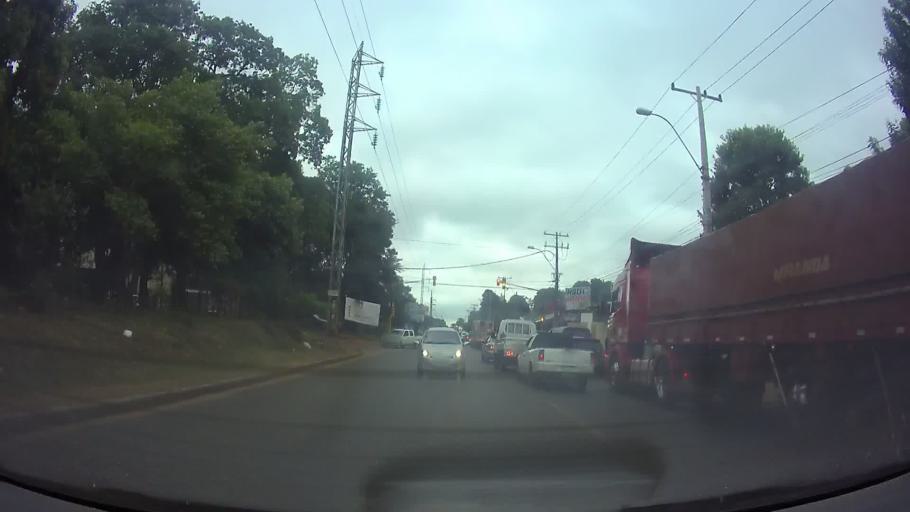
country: PY
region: Central
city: San Lorenzo
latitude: -25.3251
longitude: -57.5091
